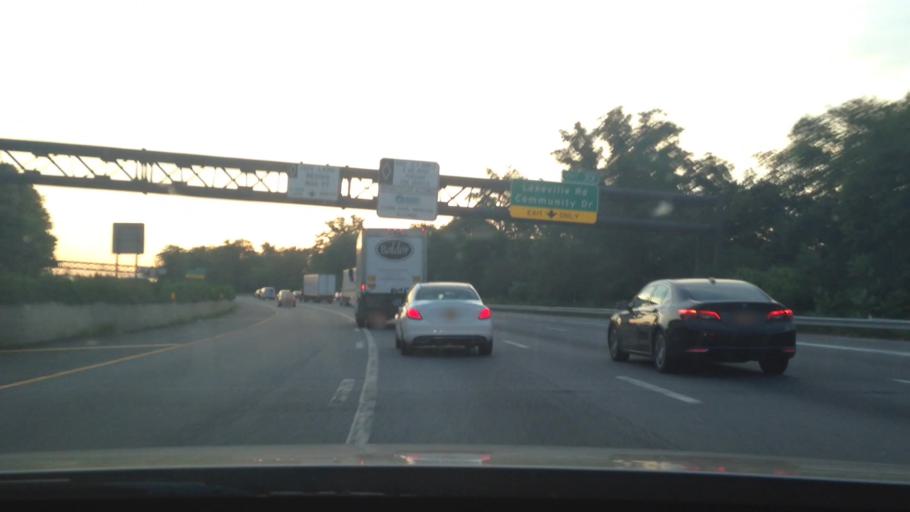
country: US
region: New York
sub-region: Nassau County
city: Lake Success
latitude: 40.7643
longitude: -73.7180
